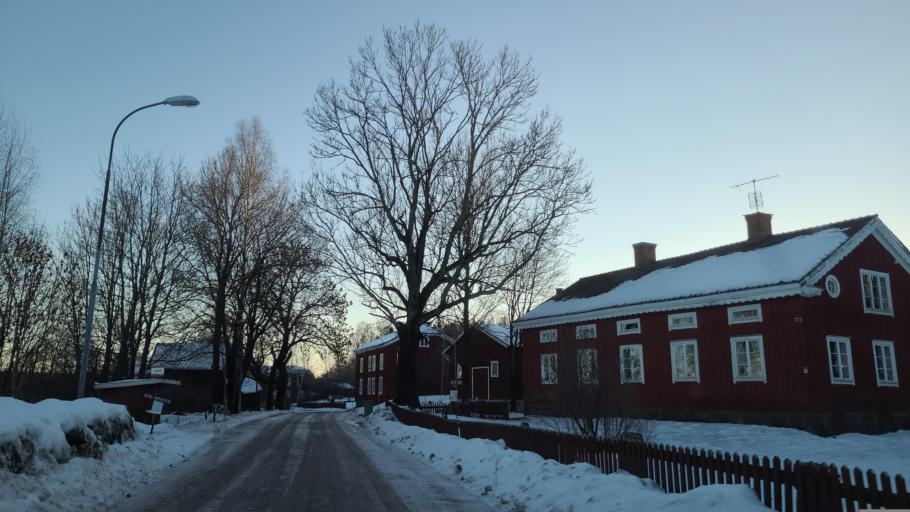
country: SE
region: Gaevleborg
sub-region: Soderhamns Kommun
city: Soderhamn
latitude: 61.2733
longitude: 16.9931
